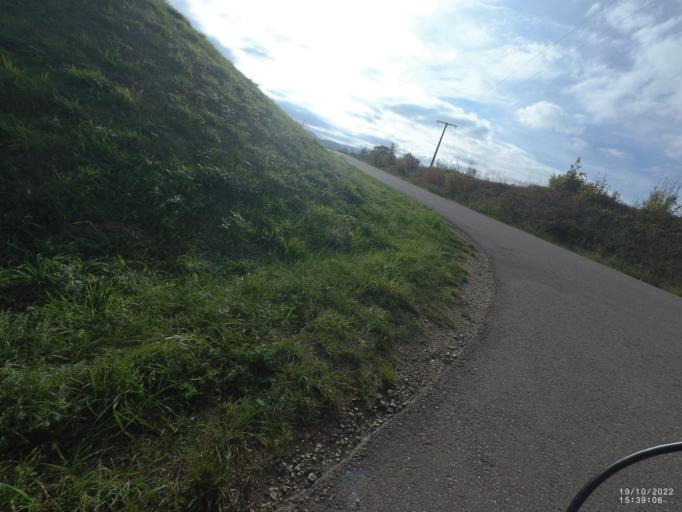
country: DE
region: Baden-Wuerttemberg
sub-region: Regierungsbezirk Stuttgart
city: Sussen
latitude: 48.6827
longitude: 9.7770
